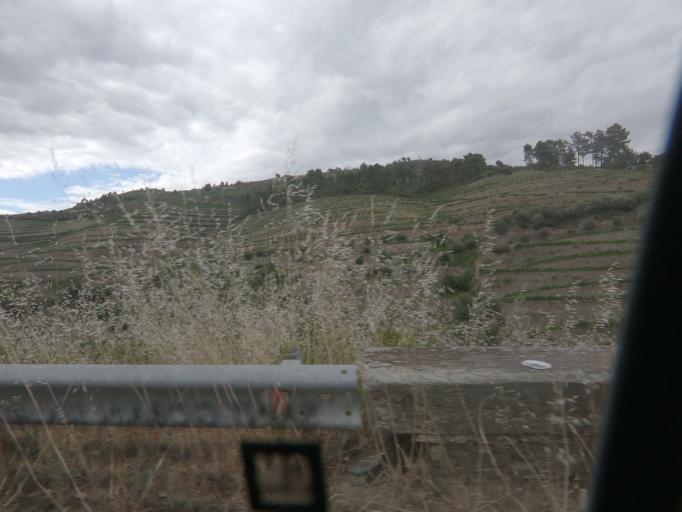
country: PT
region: Vila Real
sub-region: Sabrosa
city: Vilela
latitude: 41.1975
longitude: -7.5518
